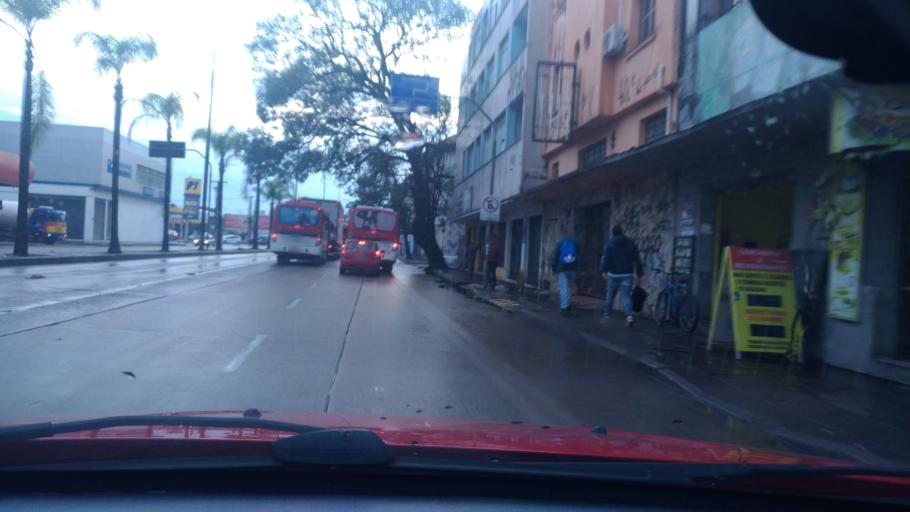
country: BR
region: Rio Grande do Sul
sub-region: Porto Alegre
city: Porto Alegre
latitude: -30.0234
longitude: -51.2133
